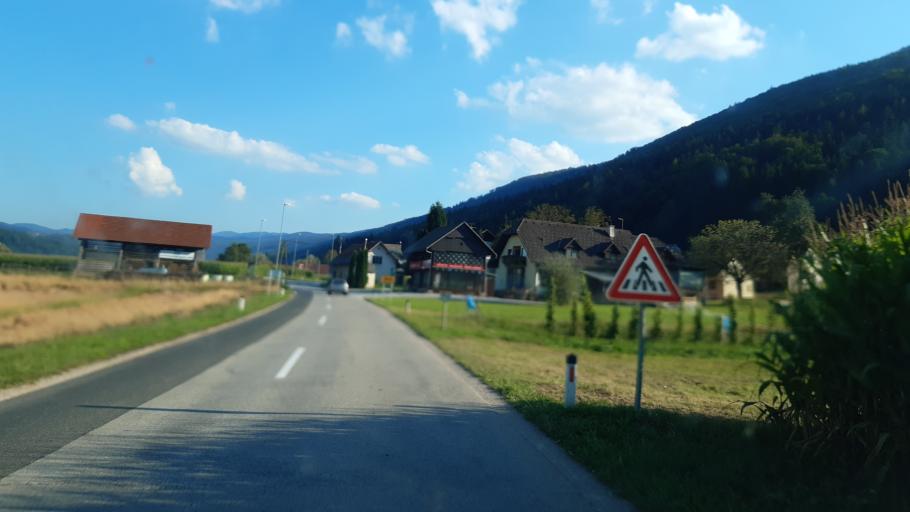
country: SI
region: Dolenjske Toplice
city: Dolenjske Toplice
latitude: 45.7525
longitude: 15.0348
